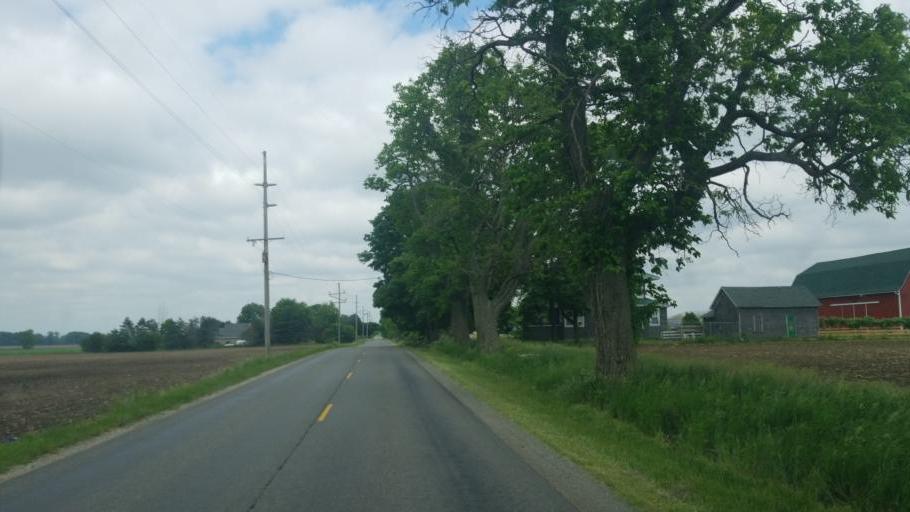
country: US
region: Indiana
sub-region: Elkhart County
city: Wakarusa
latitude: 41.4935
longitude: -86.0142
